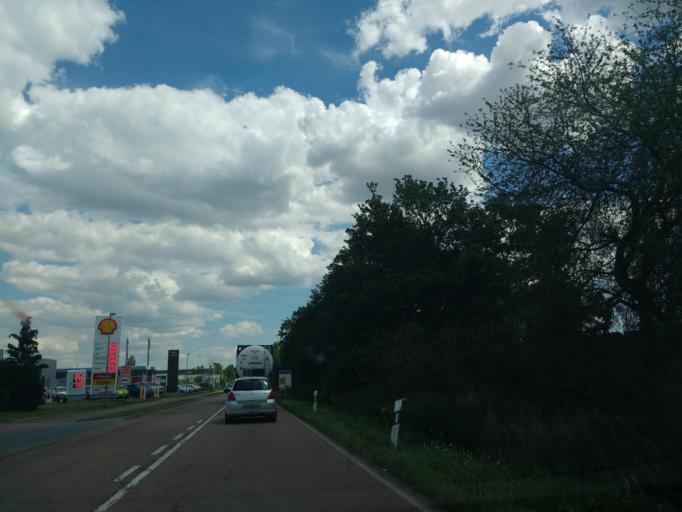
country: DE
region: Saxony-Anhalt
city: Zeitz
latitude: 51.0546
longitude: 12.1104
